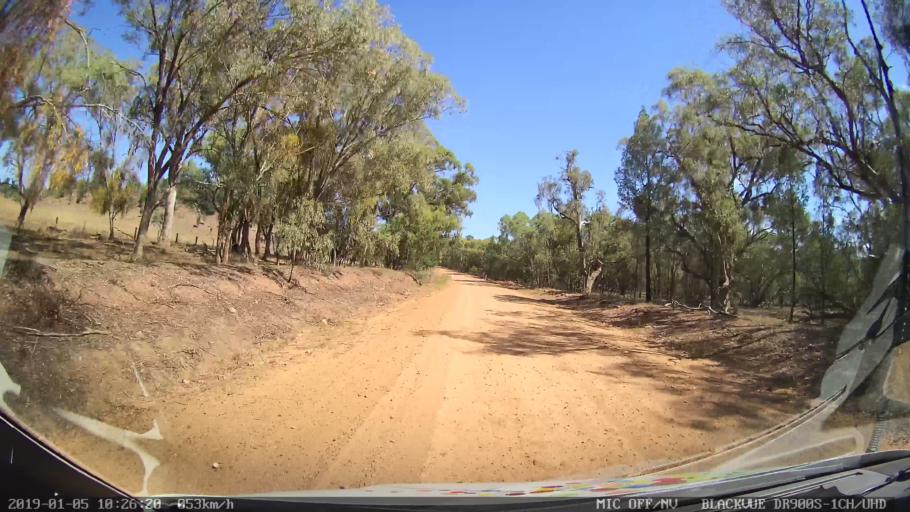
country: AU
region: New South Wales
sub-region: Gilgandra
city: Gilgandra
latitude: -31.5544
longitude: 148.9554
